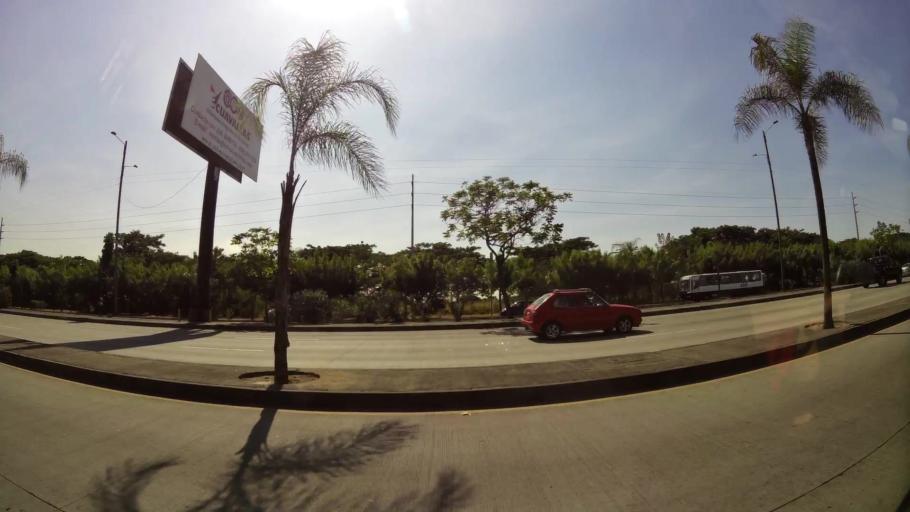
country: EC
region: Guayas
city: Eloy Alfaro
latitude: -2.1087
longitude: -79.8867
